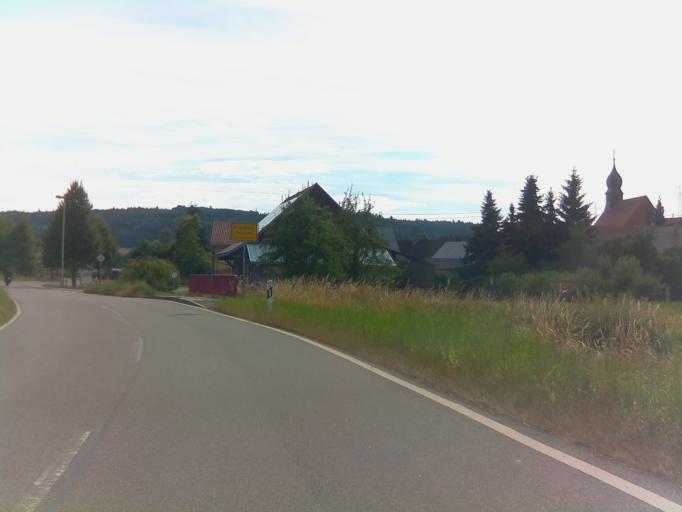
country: DE
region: Baden-Wuerttemberg
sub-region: Karlsruhe Region
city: Buchen
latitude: 49.5142
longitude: 9.3965
